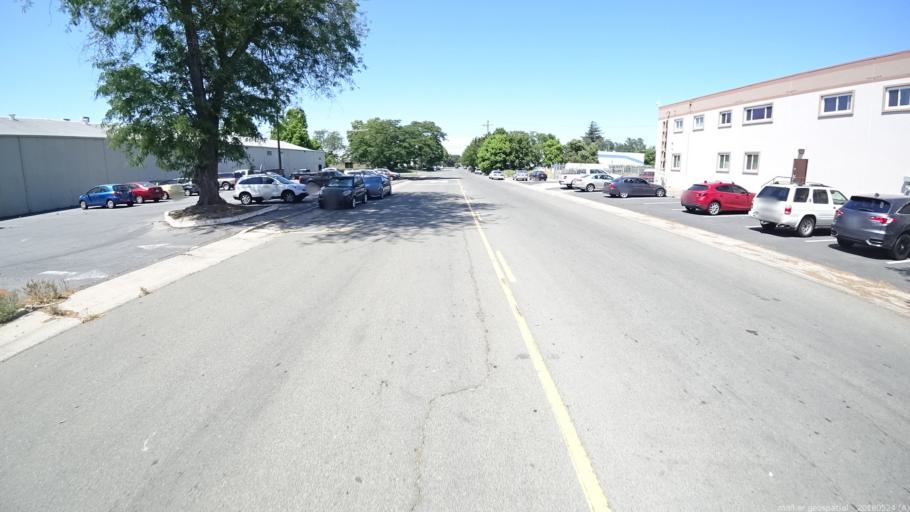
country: US
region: California
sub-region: Sacramento County
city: Sacramento
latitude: 38.5964
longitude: -121.4593
